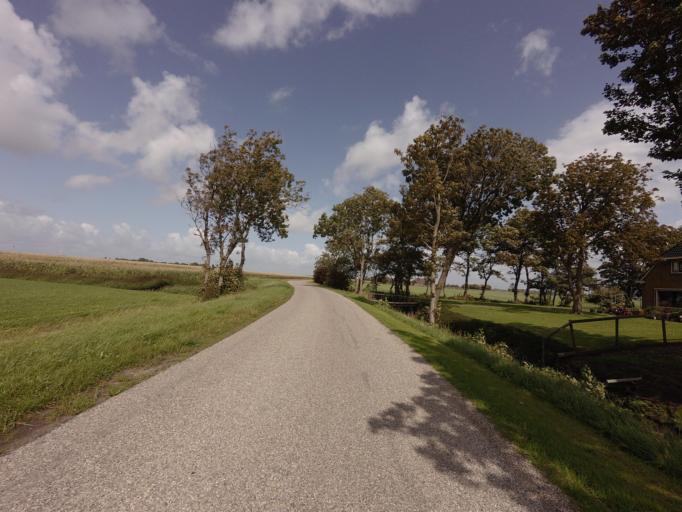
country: NL
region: Friesland
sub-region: Gemeente Harlingen
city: Harlingen
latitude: 53.1550
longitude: 5.4791
